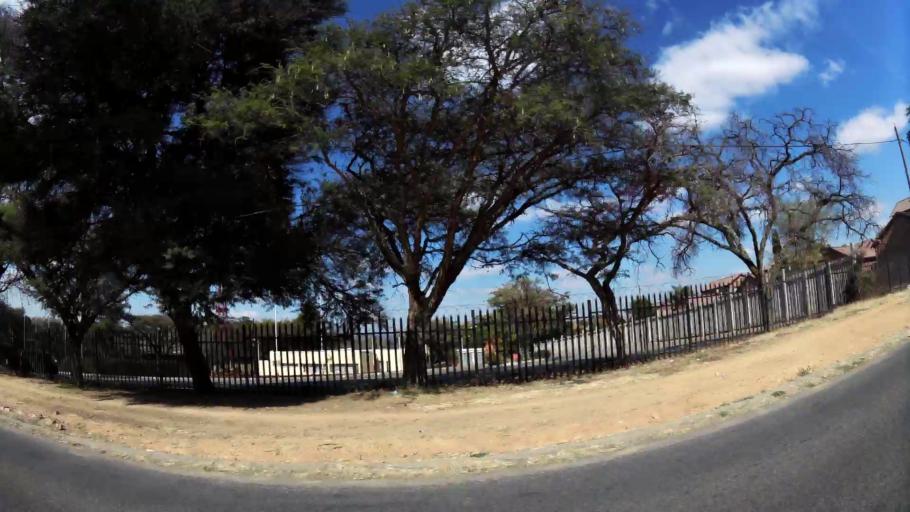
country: ZA
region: Gauteng
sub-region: City of Johannesburg Metropolitan Municipality
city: Roodepoort
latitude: -26.0809
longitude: 27.9431
